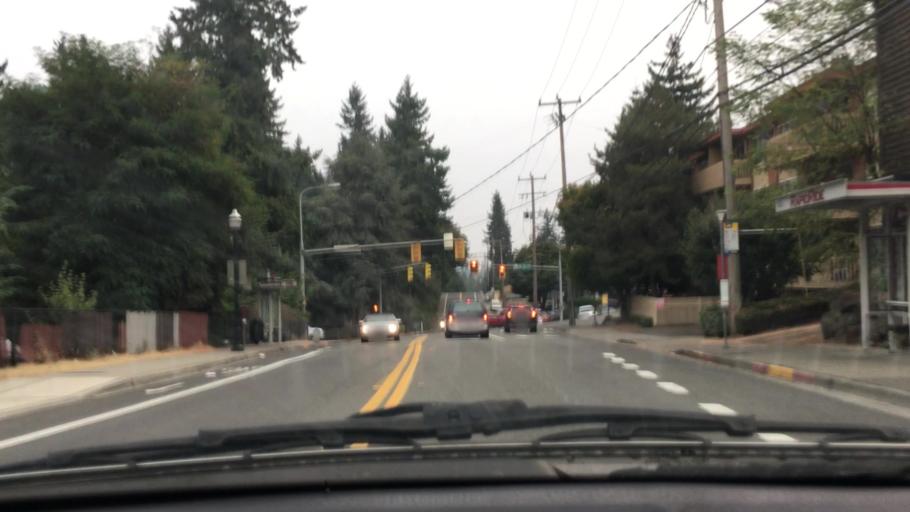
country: US
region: Washington
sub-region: King County
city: Burien
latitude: 47.4640
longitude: -122.3392
